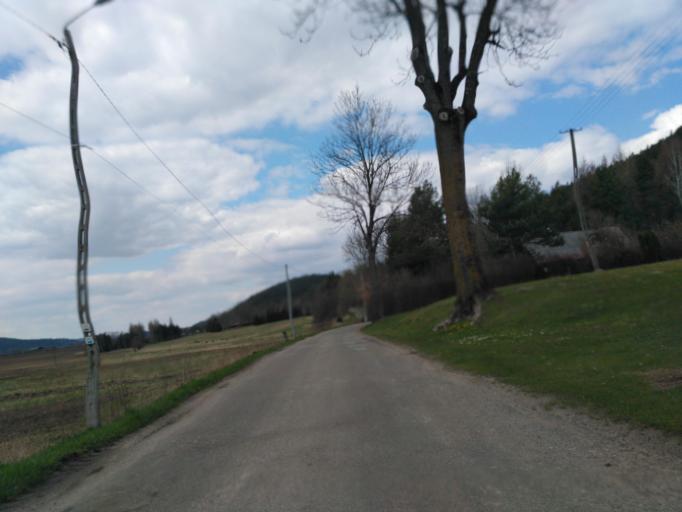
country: PL
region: Subcarpathian Voivodeship
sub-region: Powiat brzozowski
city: Dydnia
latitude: 49.6668
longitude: 22.2886
